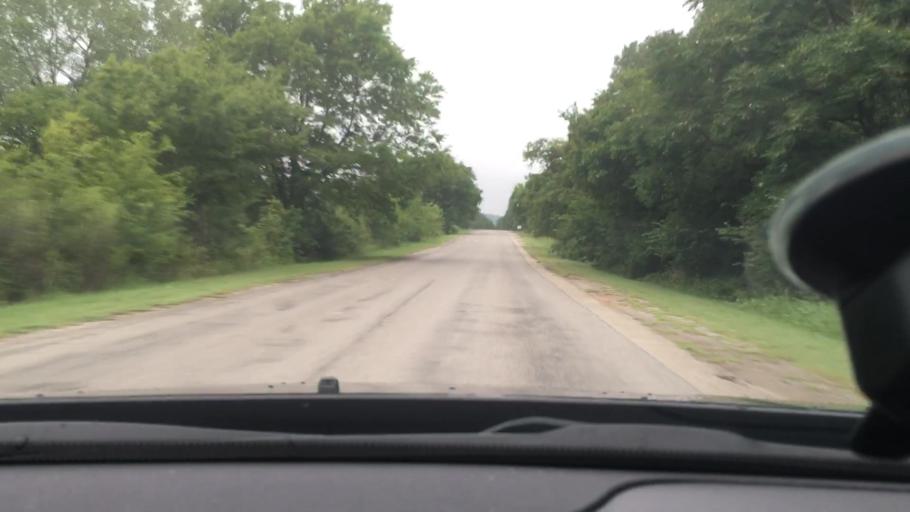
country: US
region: Oklahoma
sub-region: Murray County
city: Davis
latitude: 34.4535
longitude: -97.1356
